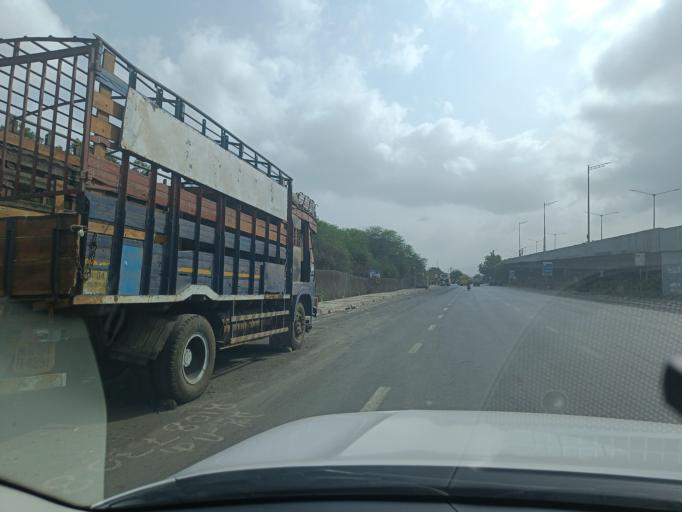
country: IN
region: Maharashtra
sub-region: Mumbai Suburban
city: Powai
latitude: 19.0826
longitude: 72.9194
